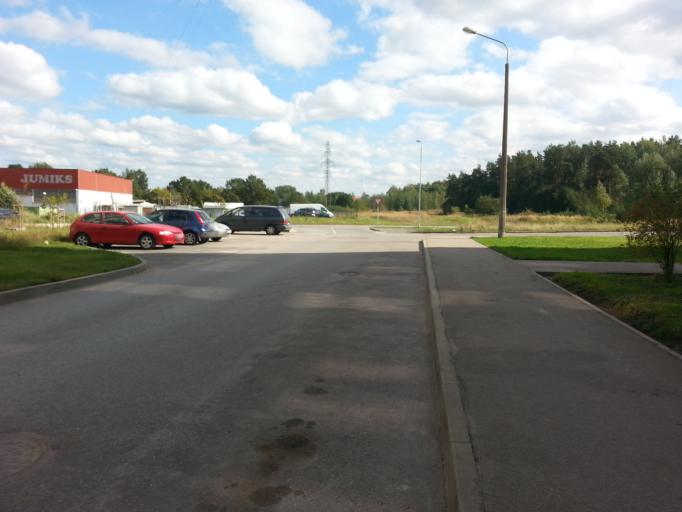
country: LV
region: Stopini
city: Ulbroka
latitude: 56.9420
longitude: 24.2298
